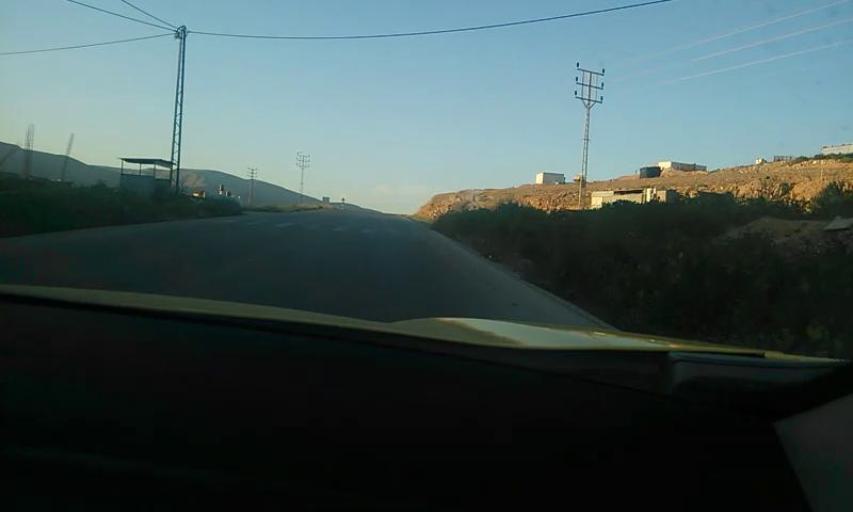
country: PS
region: West Bank
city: An Nuway`imah
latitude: 31.9030
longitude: 35.4252
